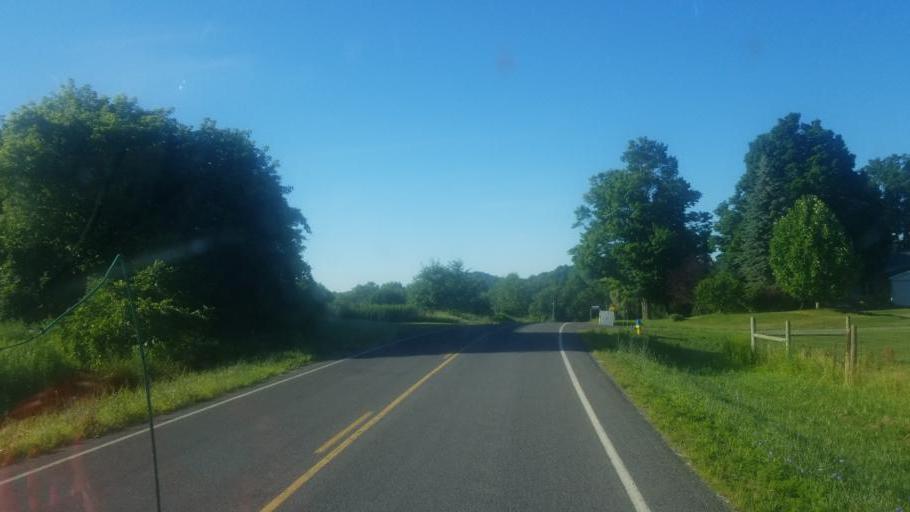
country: US
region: New York
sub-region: Wayne County
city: Lyons
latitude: 43.0913
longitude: -77.0410
